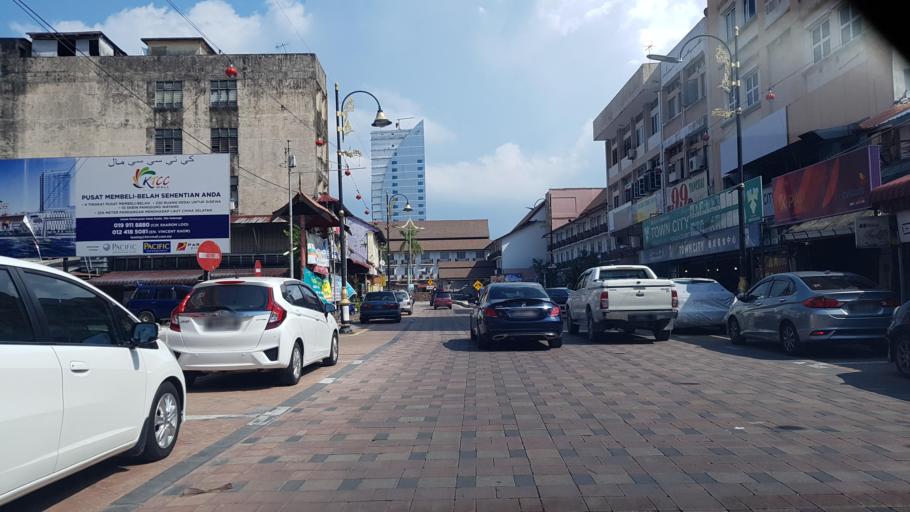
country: MY
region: Terengganu
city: Kuala Terengganu
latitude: 5.3319
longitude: 103.1325
